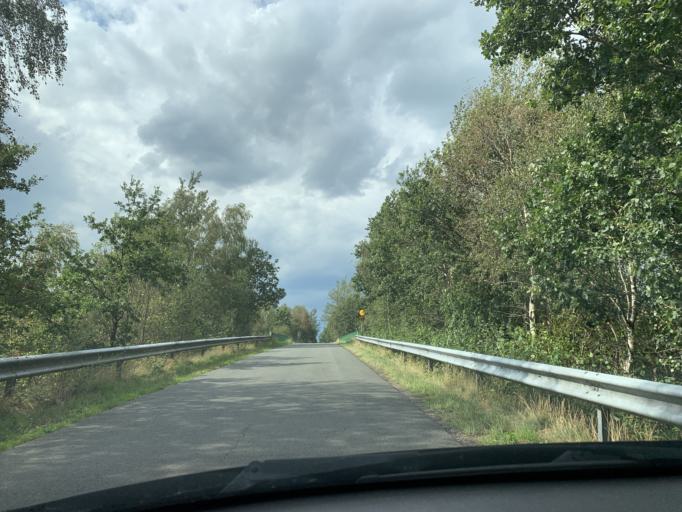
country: DE
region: Lower Saxony
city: Apen
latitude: 53.2768
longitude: 7.8187
